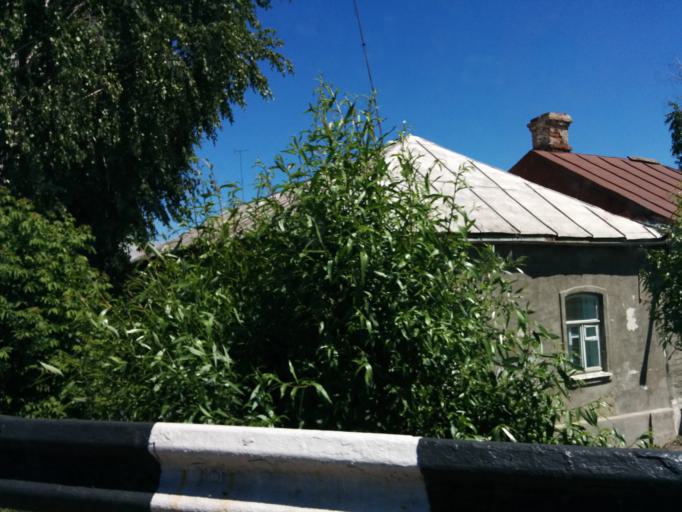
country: RU
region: Tambov
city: Morshansk
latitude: 53.4298
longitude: 41.7920
